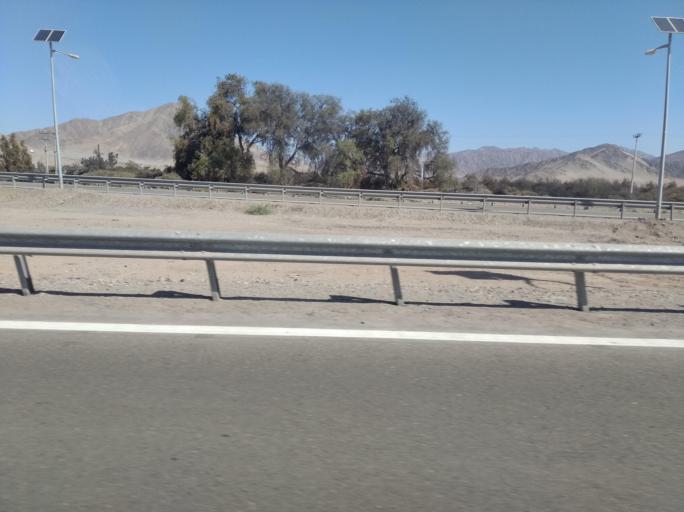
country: CL
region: Atacama
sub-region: Provincia de Copiapo
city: Copiapo
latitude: -27.3032
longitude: -70.4376
